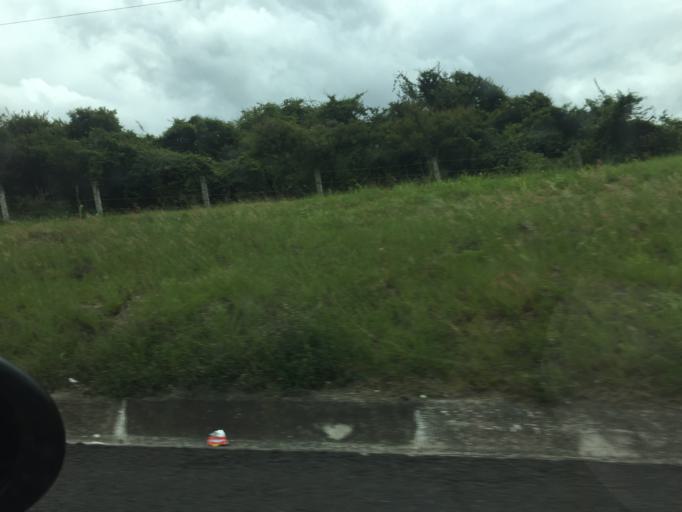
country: MX
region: Jalisco
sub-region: Zapotlanejo
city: La Mezquitera
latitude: 20.5995
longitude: -103.1169
